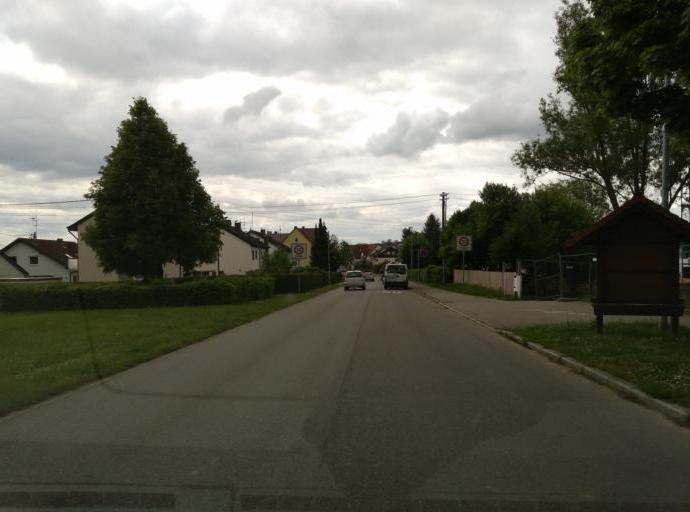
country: DE
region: Baden-Wuerttemberg
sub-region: Regierungsbezirk Stuttgart
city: Grossbettlingen
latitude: 48.6037
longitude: 9.3088
